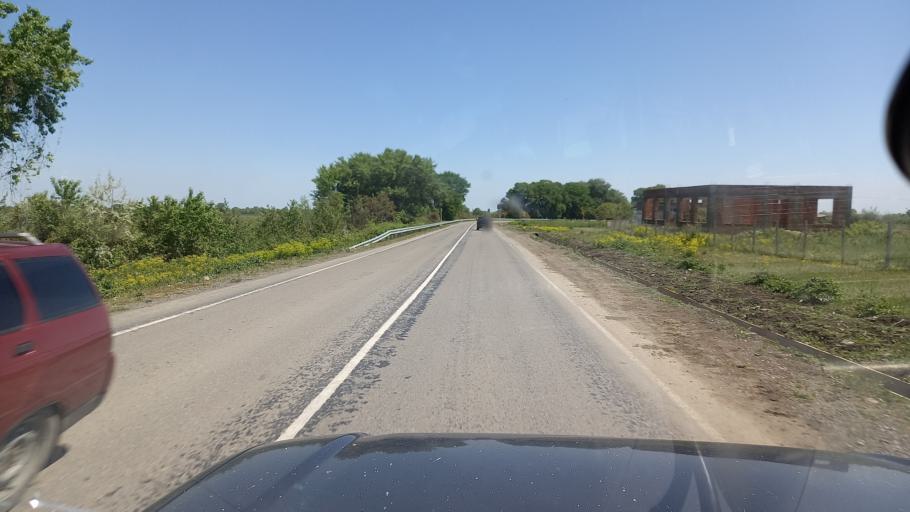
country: RU
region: Dagestan
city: Samur
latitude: 41.7324
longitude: 48.4629
